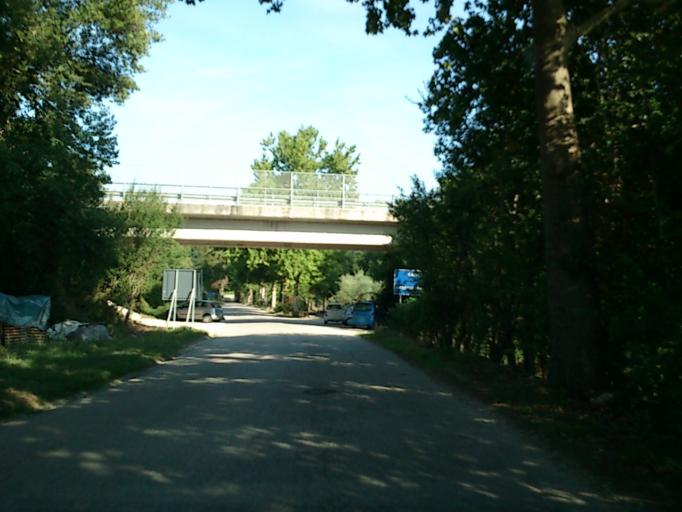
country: IT
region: The Marches
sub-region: Provincia di Pesaro e Urbino
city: Canavaccio
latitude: 43.6882
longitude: 12.7149
